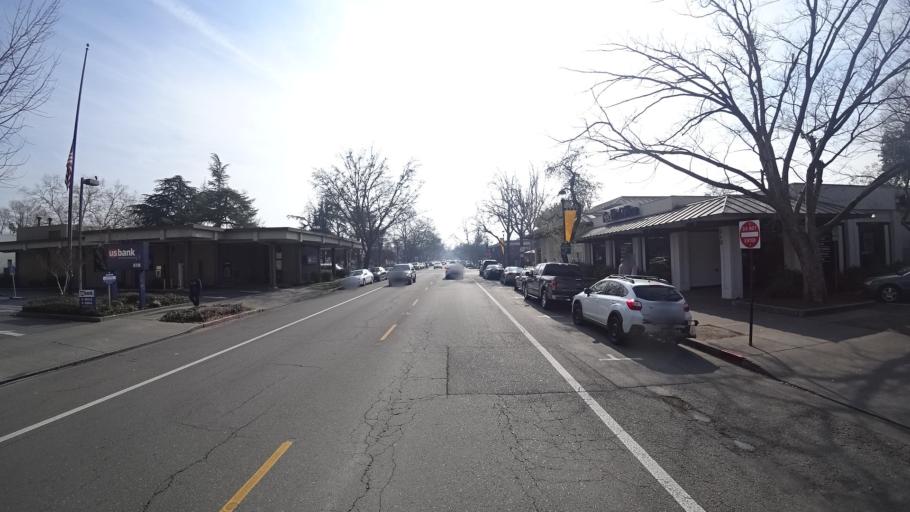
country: US
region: California
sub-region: Yolo County
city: Davis
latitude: 38.5453
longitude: -121.7405
